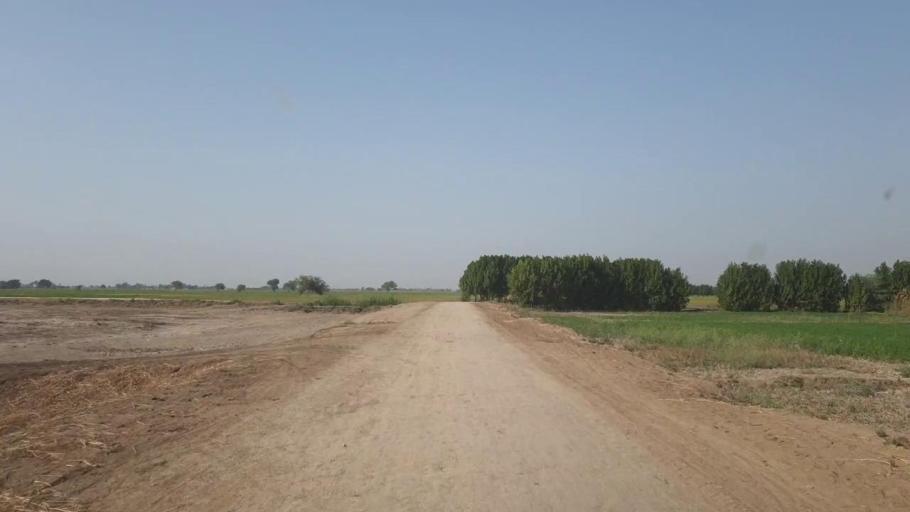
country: PK
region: Sindh
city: Kario
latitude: 24.5812
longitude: 68.5441
